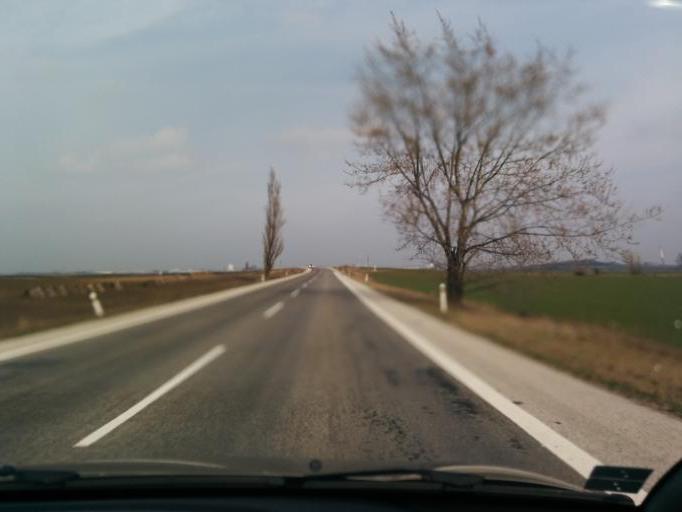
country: SK
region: Trnavsky
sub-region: Okres Galanta
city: Galanta
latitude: 48.2534
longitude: 17.7092
